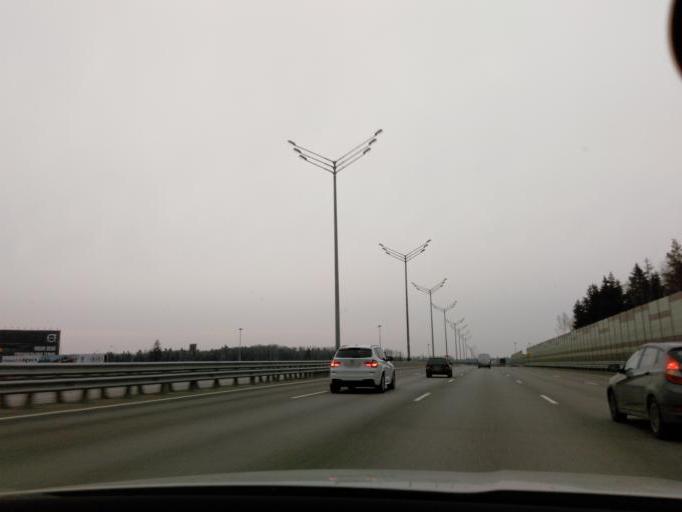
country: RU
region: Moskovskaya
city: Novopodrezkovo
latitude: 55.9587
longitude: 37.4070
